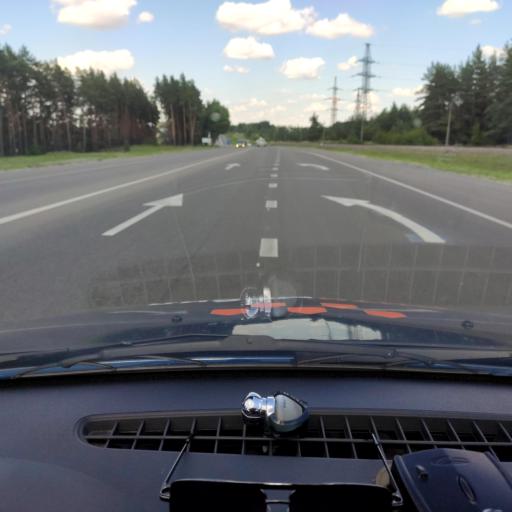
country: RU
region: Voronezj
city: Novovoronezh
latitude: 51.3321
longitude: 39.2554
